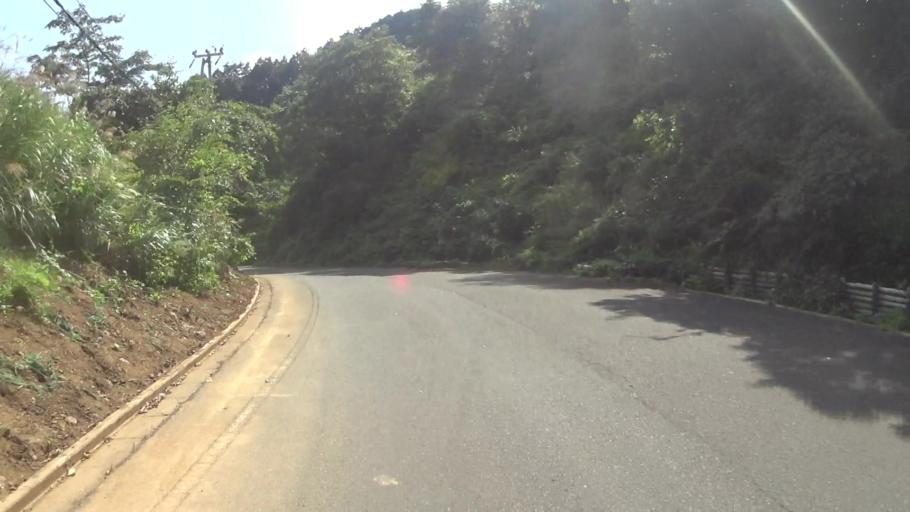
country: JP
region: Kyoto
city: Miyazu
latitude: 35.7177
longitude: 135.1939
